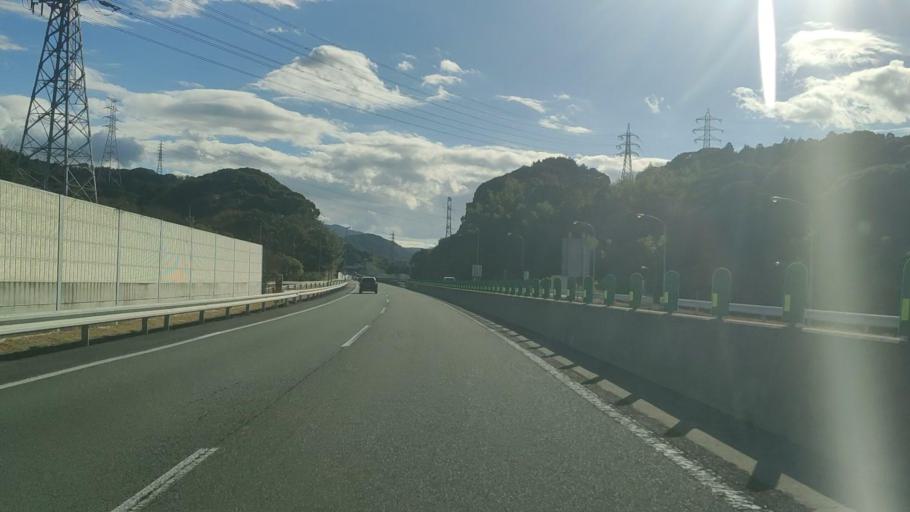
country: JP
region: Fukuoka
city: Kitakyushu
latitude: 33.8408
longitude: 130.7654
